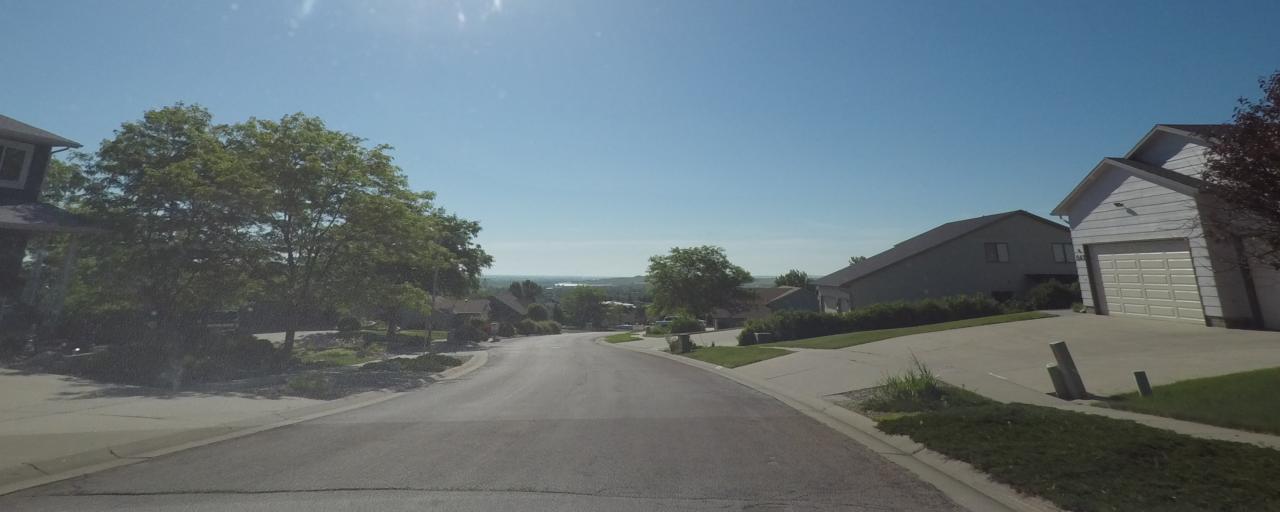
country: US
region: South Dakota
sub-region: Pennington County
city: Rapid City
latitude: 44.0509
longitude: -103.2279
